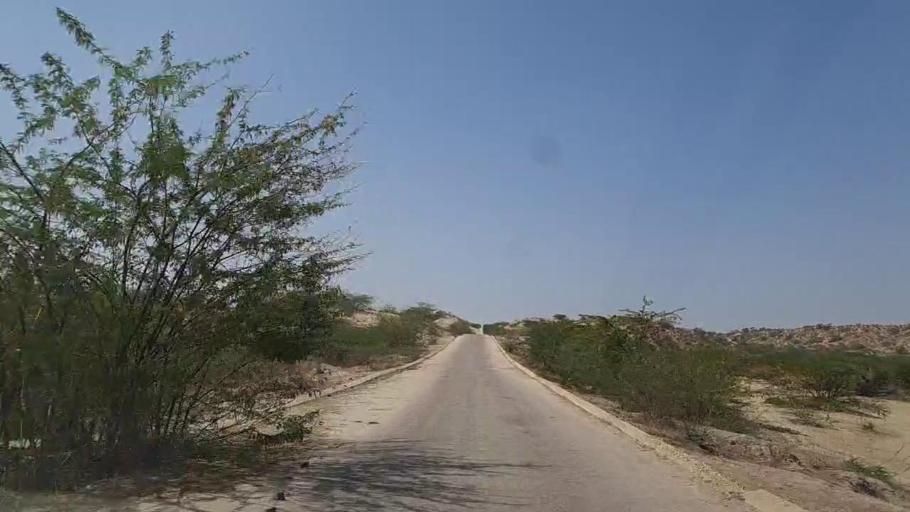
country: PK
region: Sindh
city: Diplo
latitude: 24.5239
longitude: 69.3649
